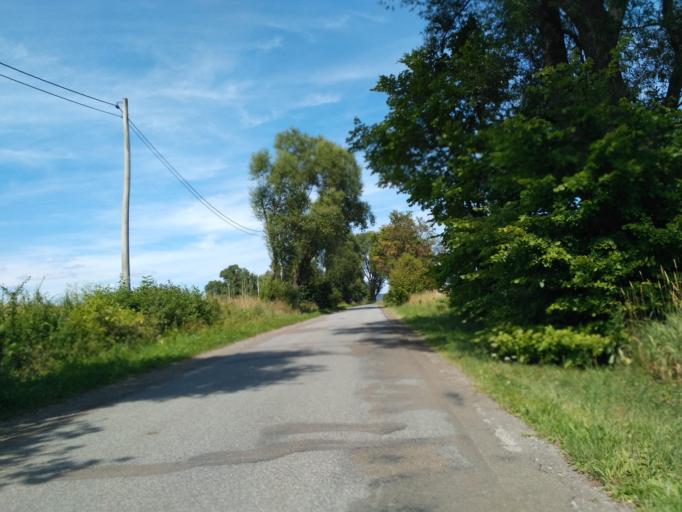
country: PL
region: Subcarpathian Voivodeship
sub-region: Powiat sanocki
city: Strachocina
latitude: 49.5703
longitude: 22.1213
